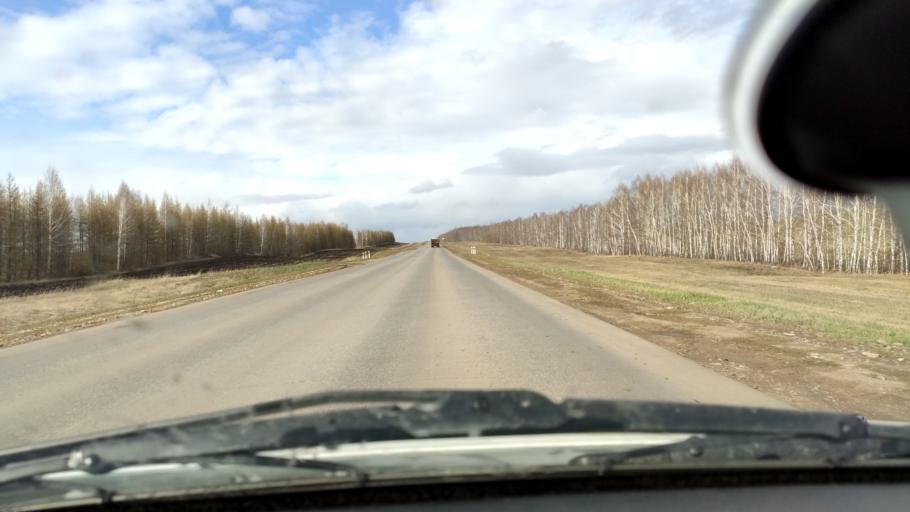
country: RU
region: Bashkortostan
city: Buzdyak
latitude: 54.6972
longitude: 54.5607
